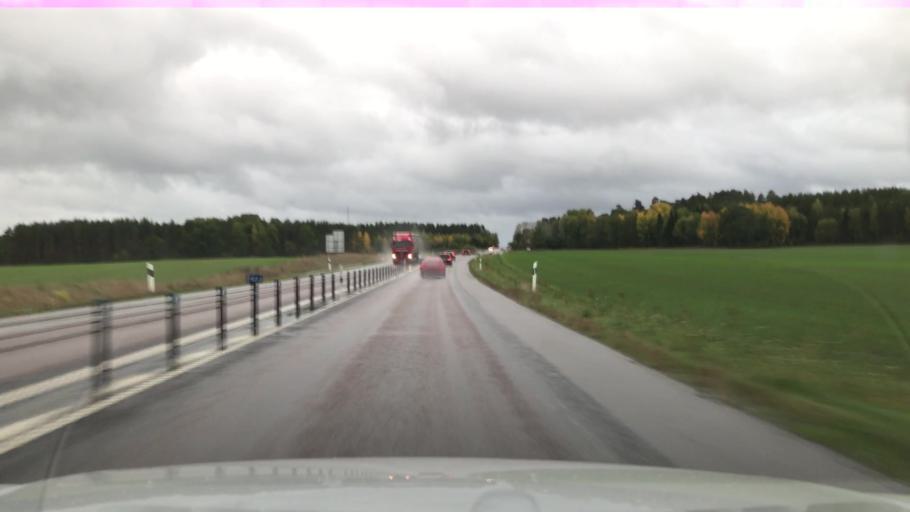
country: SE
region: OEstergoetland
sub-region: Soderkopings Kommun
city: Soederkoeping
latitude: 58.5276
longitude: 16.2871
